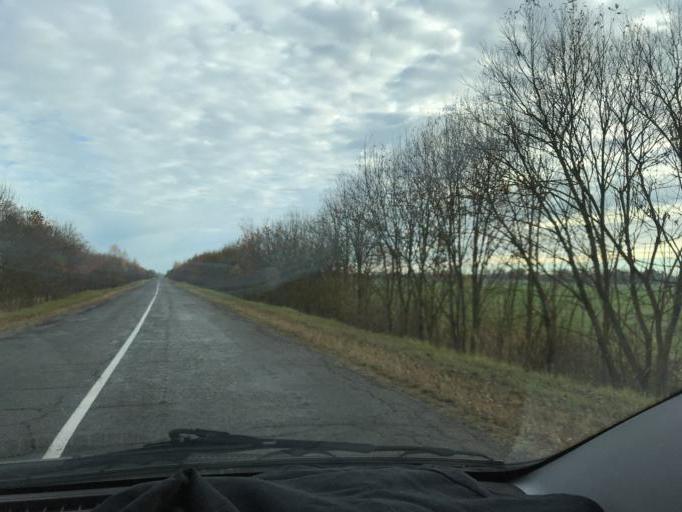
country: BY
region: Vitebsk
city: Haradok
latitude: 55.4045
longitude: 29.7324
